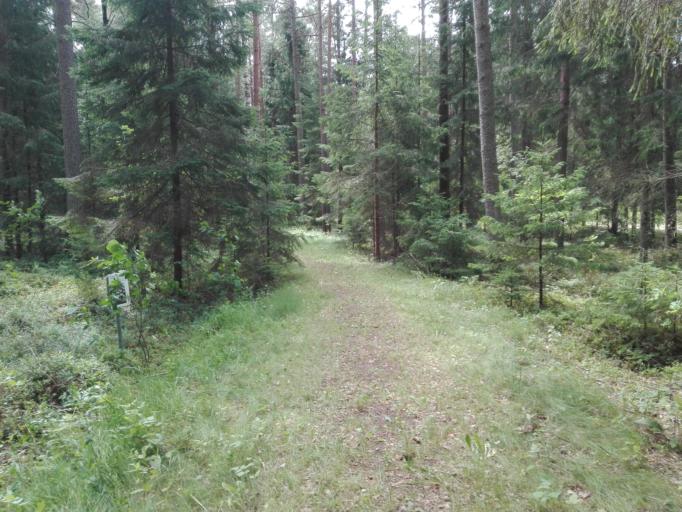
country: LT
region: Panevezys
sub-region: Birzai
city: Birzai
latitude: 56.2680
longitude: 24.7525
